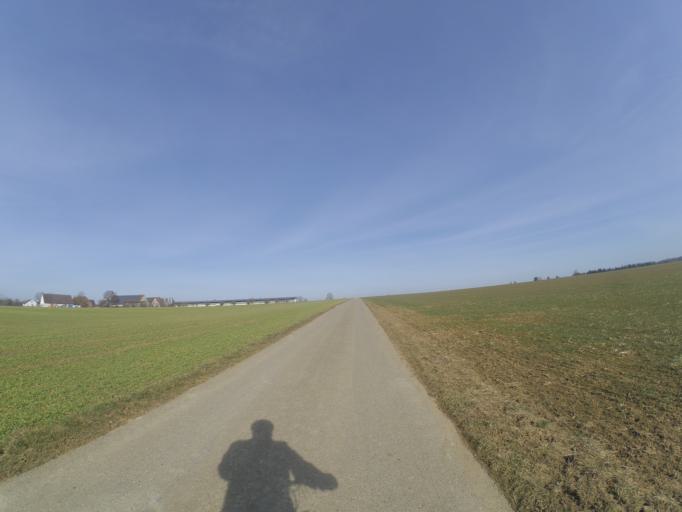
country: DE
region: Baden-Wuerttemberg
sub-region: Tuebingen Region
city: Beimerstetten
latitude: 48.4675
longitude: 9.9965
